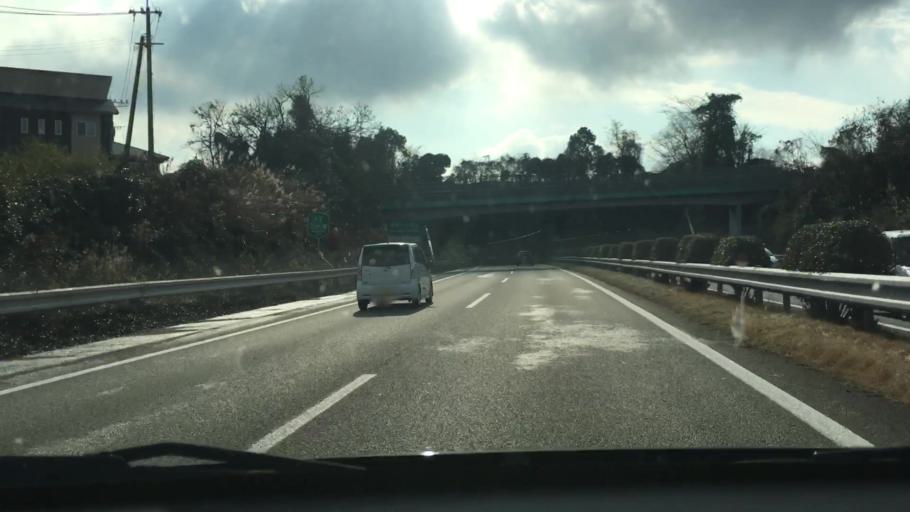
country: JP
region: Kumamoto
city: Uto
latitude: 32.6915
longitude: 130.7387
